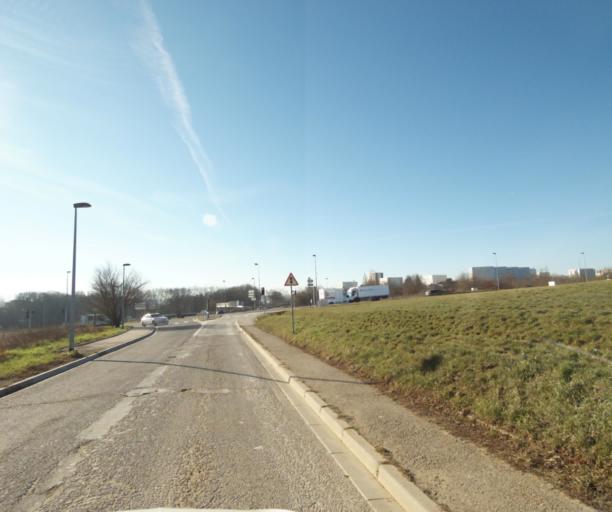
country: FR
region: Lorraine
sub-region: Departement de Meurthe-et-Moselle
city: Laxou
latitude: 48.7062
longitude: 6.1355
